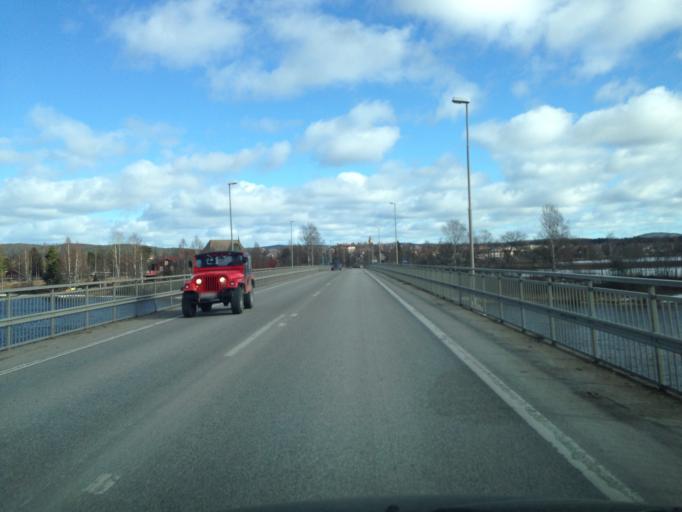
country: SE
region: Gaevleborg
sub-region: Ljusdals Kommun
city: Ljusdal
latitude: 61.8236
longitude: 16.0659
